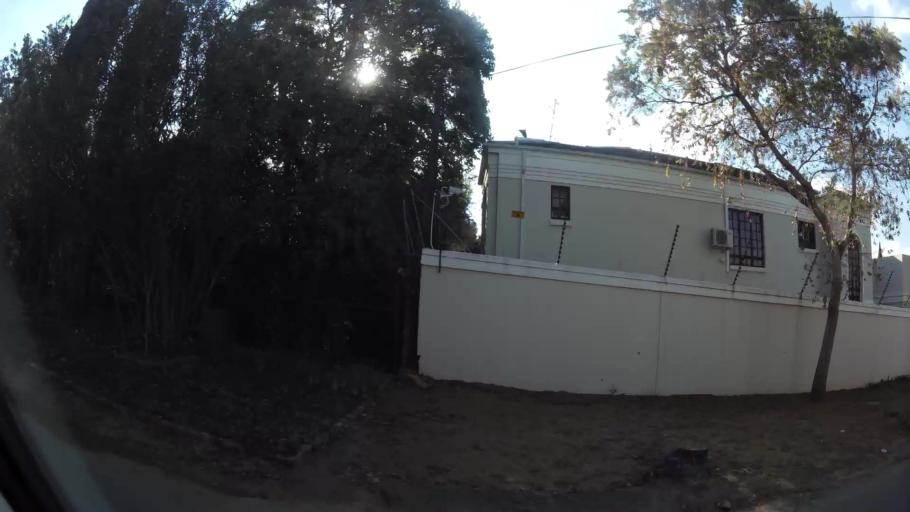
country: ZA
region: Gauteng
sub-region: City of Johannesburg Metropolitan Municipality
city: Diepsloot
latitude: -26.0220
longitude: 28.0249
